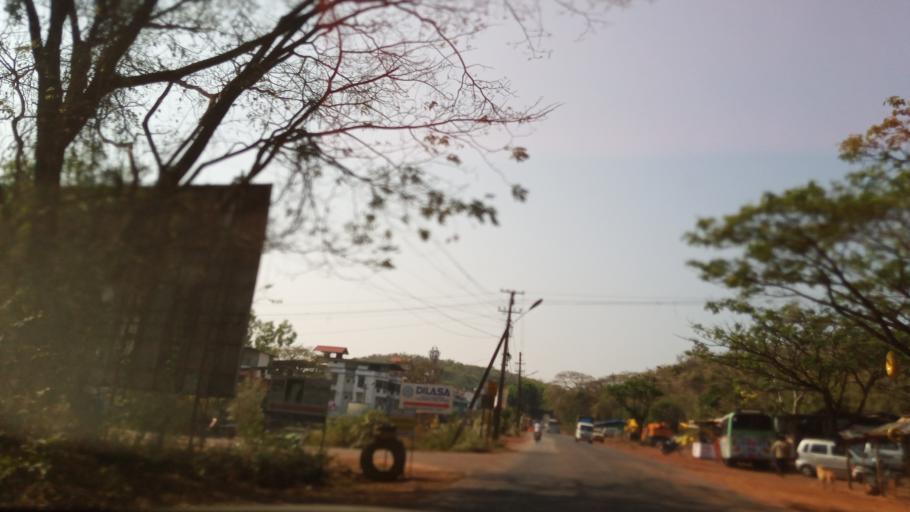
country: IN
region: Goa
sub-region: North Goa
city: Bandora
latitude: 15.4102
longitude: 73.9914
